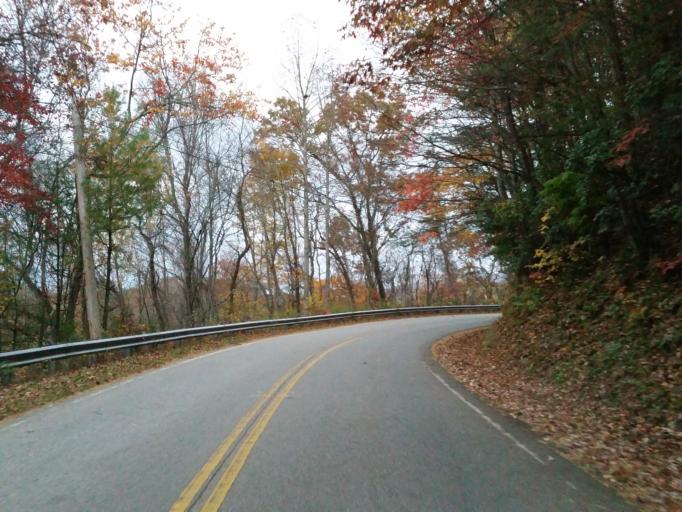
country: US
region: Georgia
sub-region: Lumpkin County
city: Dahlonega
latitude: 34.7041
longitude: -84.0417
